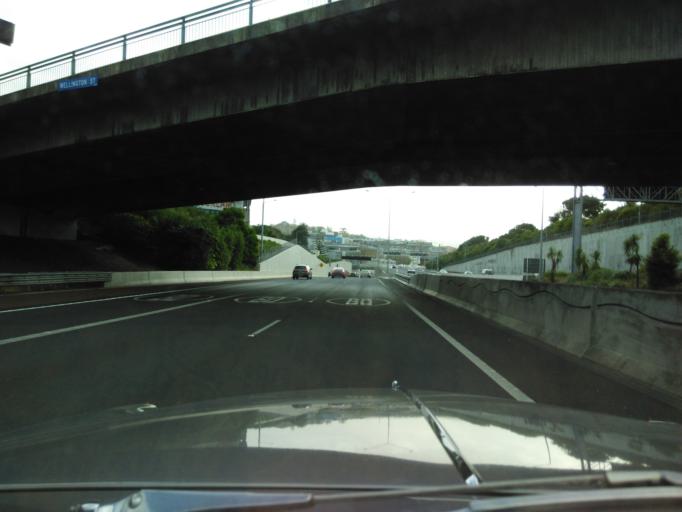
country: NZ
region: Auckland
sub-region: Auckland
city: Auckland
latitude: -36.8533
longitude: 174.7559
